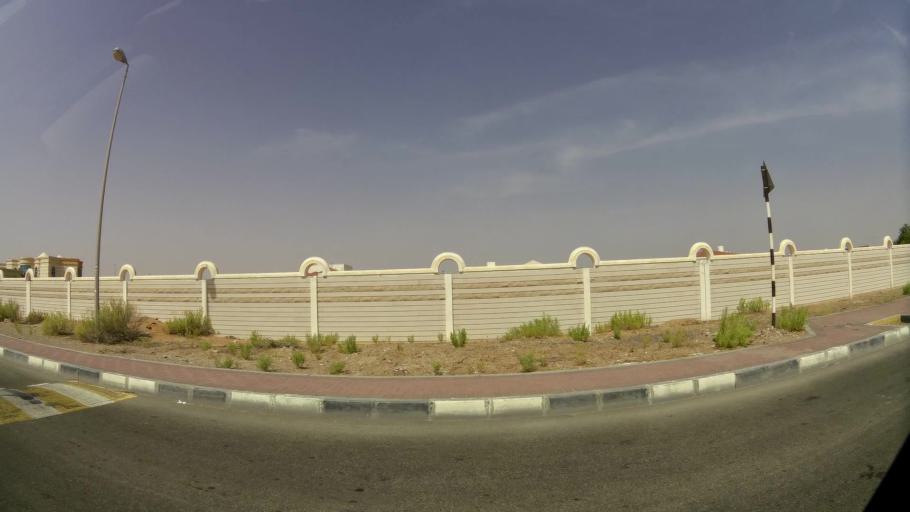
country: AE
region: Abu Dhabi
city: Al Ain
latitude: 24.1603
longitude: 55.6776
